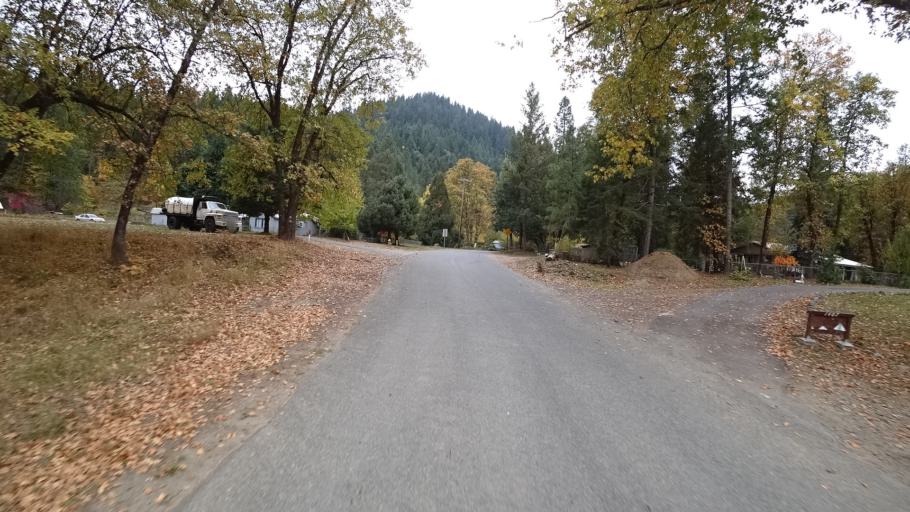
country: US
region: California
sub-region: Siskiyou County
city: Happy Camp
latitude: 41.7782
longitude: -123.3927
